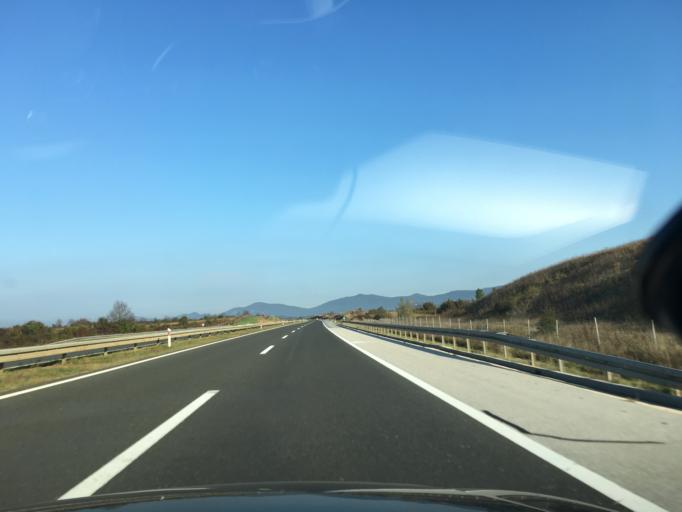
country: HR
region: Licko-Senjska
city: Gospic
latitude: 44.4943
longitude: 15.5380
